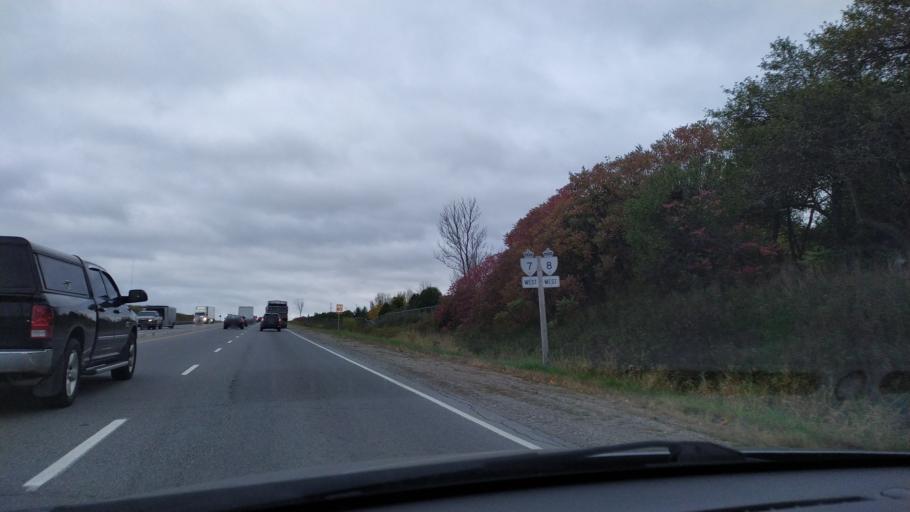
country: CA
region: Ontario
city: Kitchener
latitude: 43.3723
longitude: -80.7037
